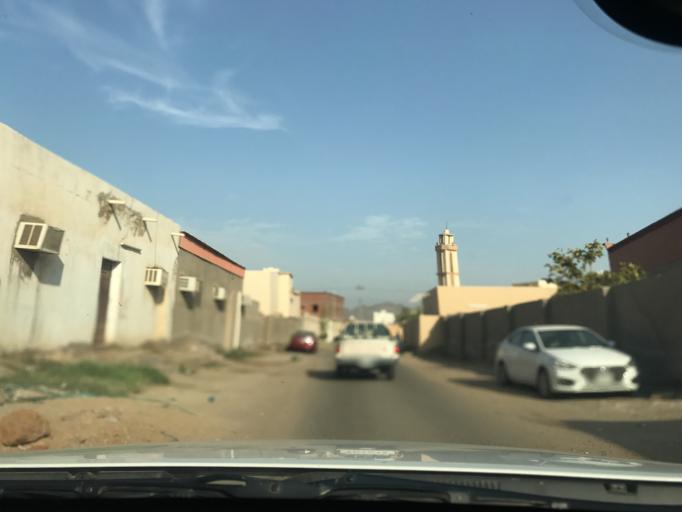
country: SA
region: Makkah
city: Al Jumum
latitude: 21.4409
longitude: 39.5216
